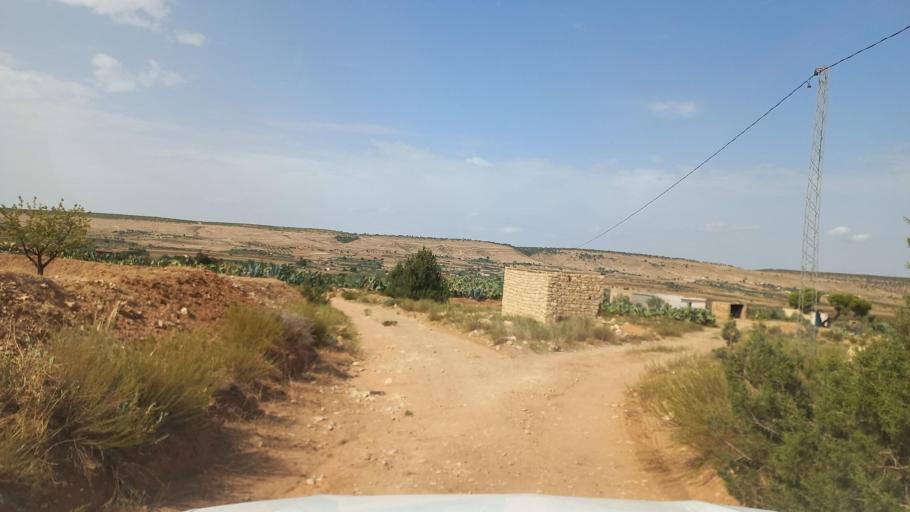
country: TN
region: Al Qasrayn
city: Kasserine
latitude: 35.3497
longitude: 8.8680
